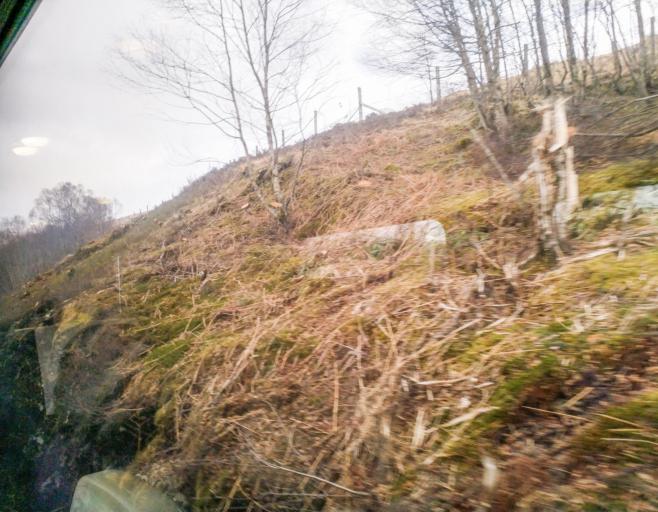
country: GB
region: Scotland
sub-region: Highland
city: Spean Bridge
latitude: 56.7850
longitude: -4.7319
